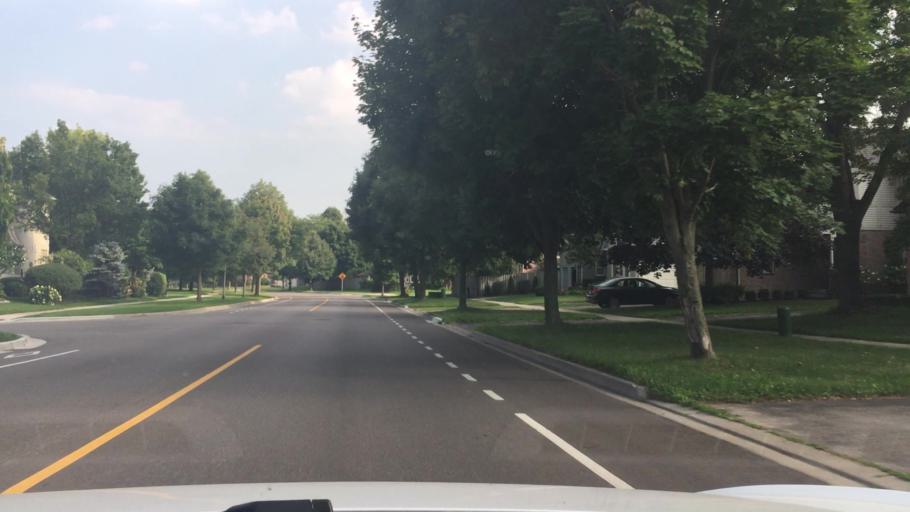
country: CA
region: Ontario
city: Ajax
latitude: 43.8812
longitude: -78.9664
